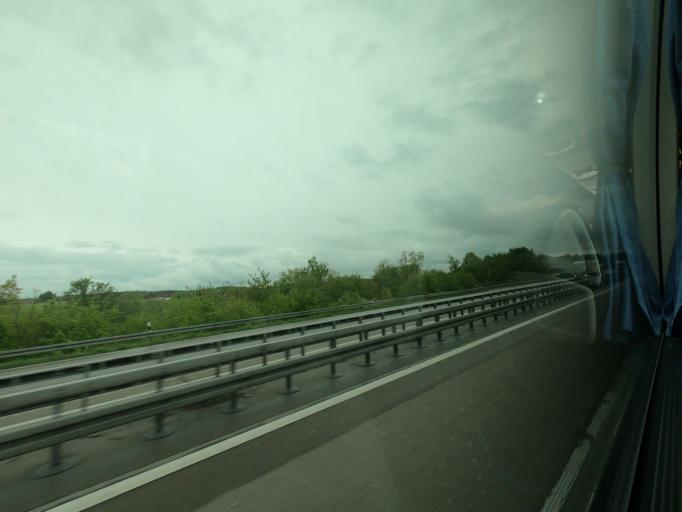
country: DE
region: Baden-Wuerttemberg
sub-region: Regierungsbezirk Stuttgart
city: Kirchberg an der Jagst
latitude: 49.1733
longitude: 10.0009
